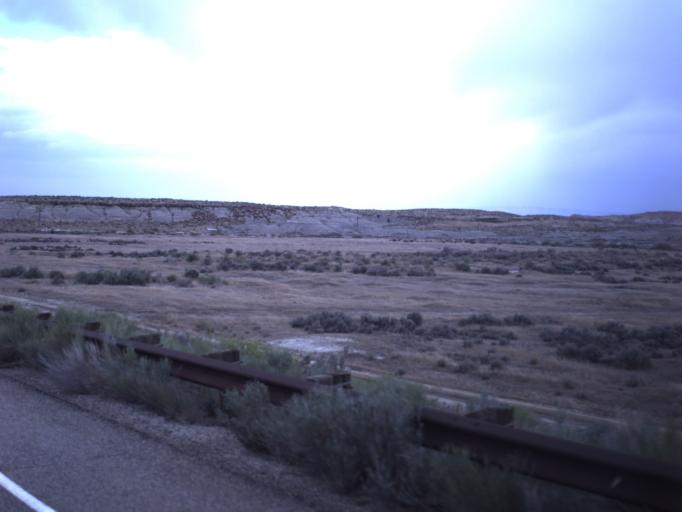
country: US
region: Colorado
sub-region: Rio Blanco County
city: Rangely
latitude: 40.0911
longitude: -109.2232
